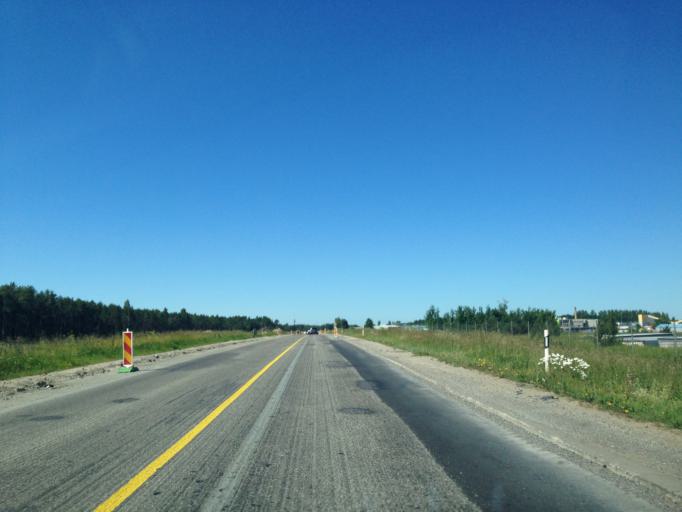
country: EE
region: Harju
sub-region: Rae vald
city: Jueri
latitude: 59.3945
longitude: 24.9183
